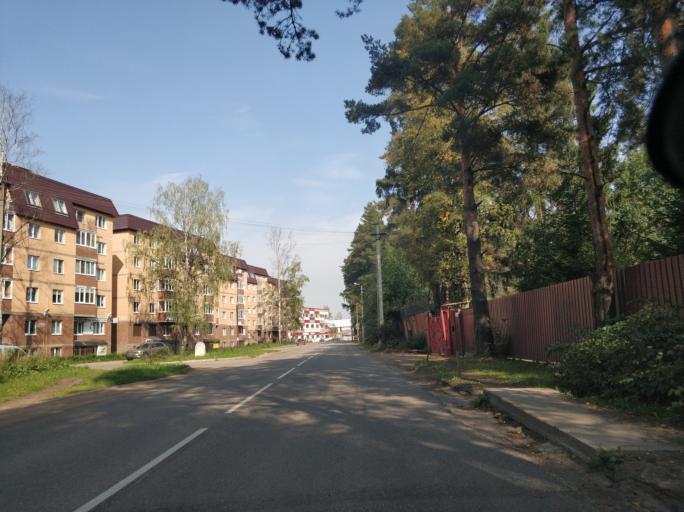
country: RU
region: Leningrad
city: Vsevolozhsk
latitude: 60.0154
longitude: 30.6229
